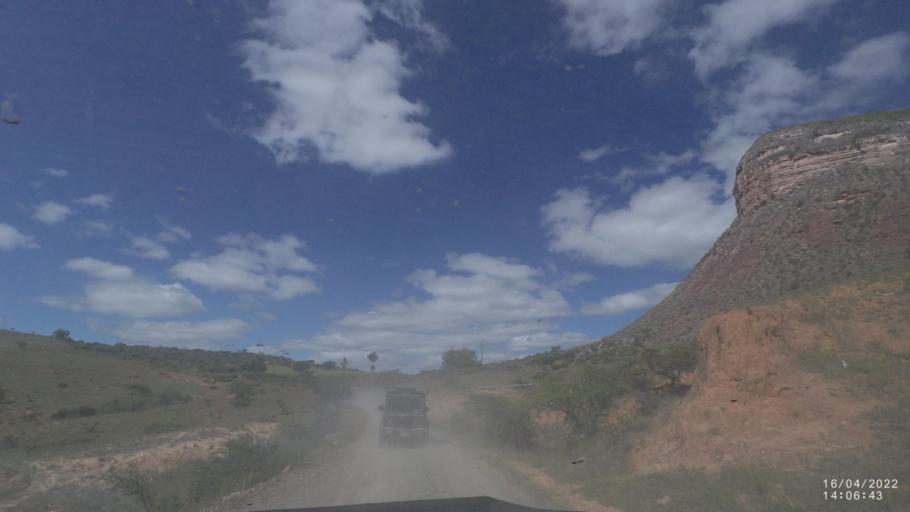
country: BO
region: Cochabamba
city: Mizque
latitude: -18.0576
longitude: -65.5303
